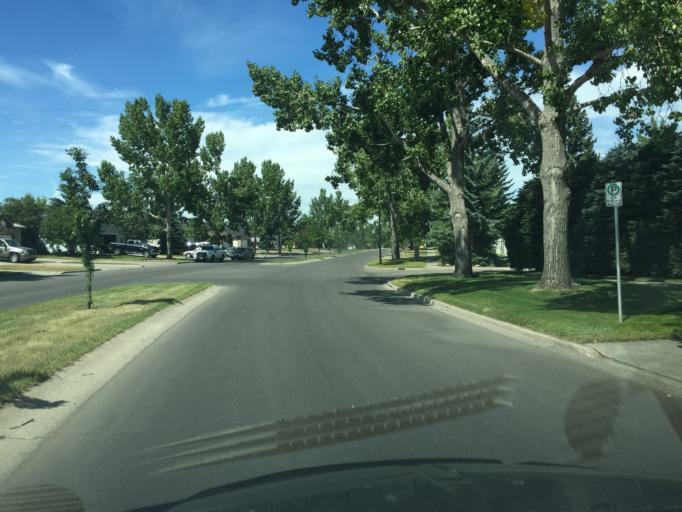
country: CA
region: Alberta
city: Calgary
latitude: 50.9338
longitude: -114.0647
